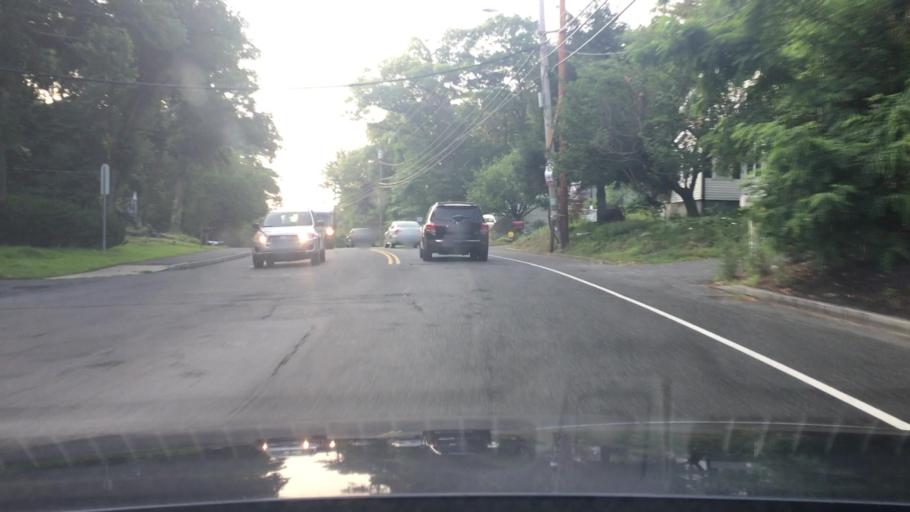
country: US
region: Massachusetts
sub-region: Essex County
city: Saugus
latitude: 42.4853
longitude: -71.0134
